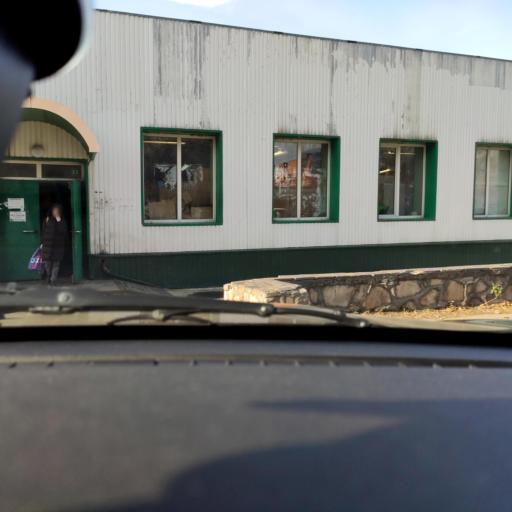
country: RU
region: Samara
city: Tol'yatti
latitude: 53.5073
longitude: 49.4041
